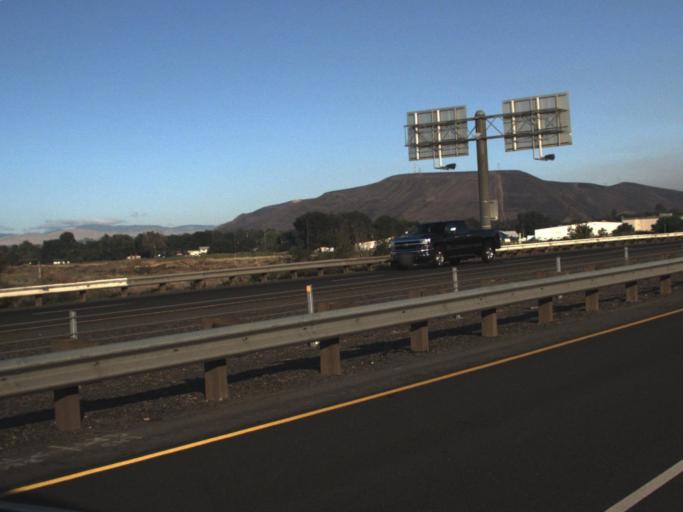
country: US
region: Washington
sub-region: Yakima County
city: Yakima
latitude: 46.6200
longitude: -120.4959
